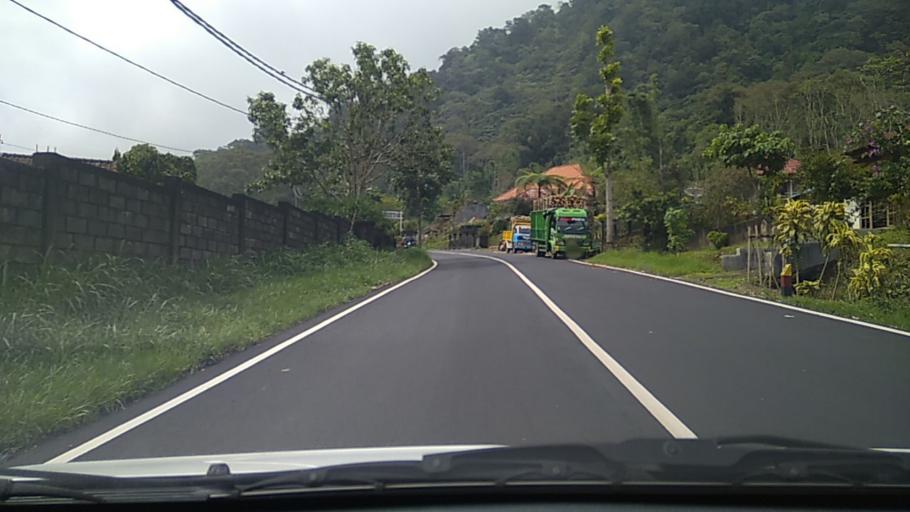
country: ID
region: Bali
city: Munduk
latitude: -8.2431
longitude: 115.1487
